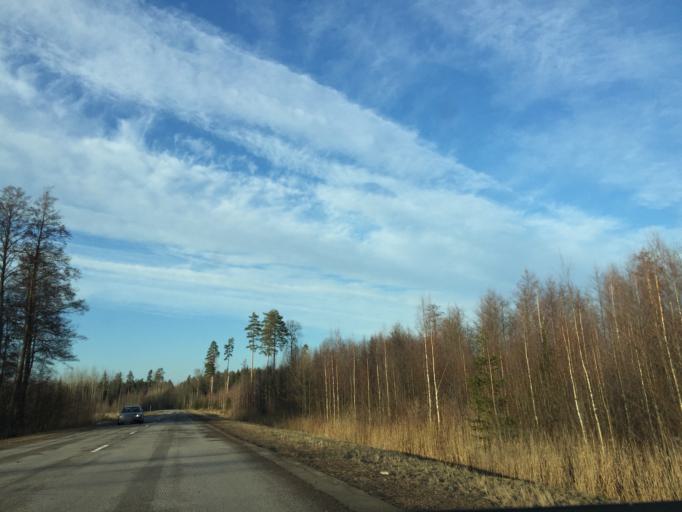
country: LV
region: Kekava
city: Balozi
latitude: 56.8192
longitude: 24.0622
